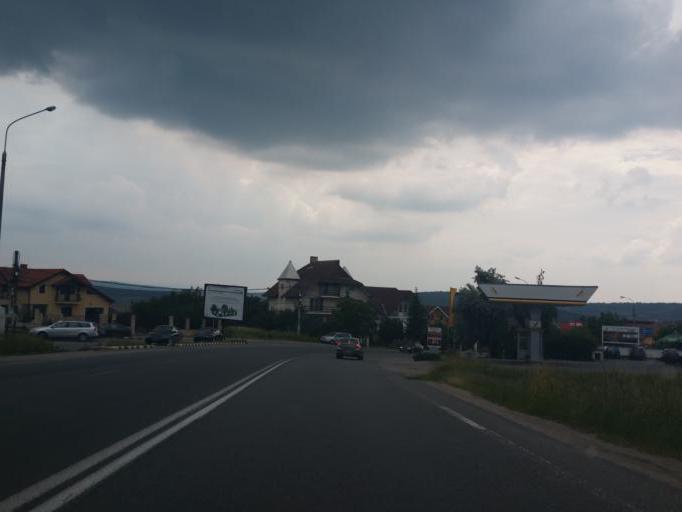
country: RO
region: Salaj
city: Zalau
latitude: 47.1676
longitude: 23.0758
